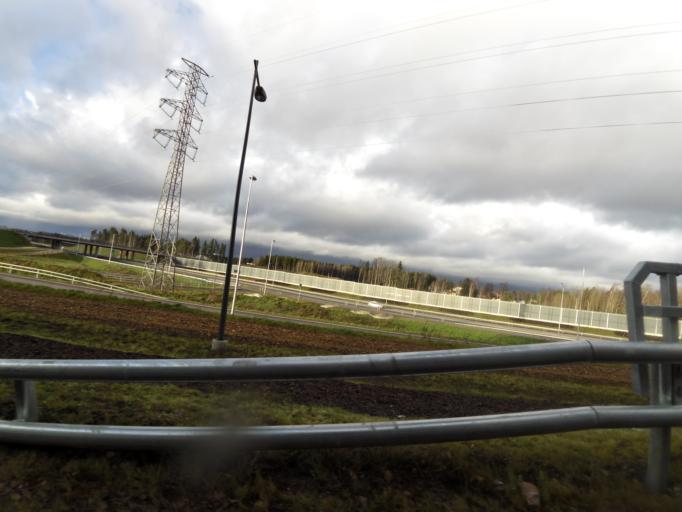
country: FI
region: Uusimaa
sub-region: Helsinki
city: Kilo
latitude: 60.2064
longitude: 24.7885
